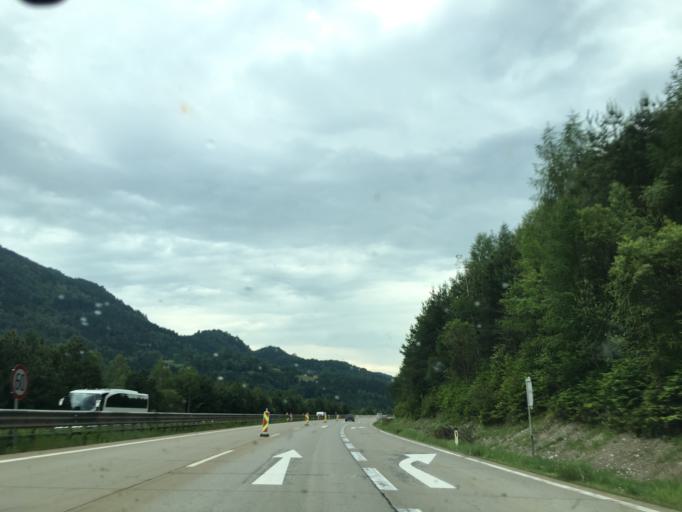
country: AT
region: Carinthia
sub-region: Villach Stadt
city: Villach
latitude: 46.6443
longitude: 13.7909
